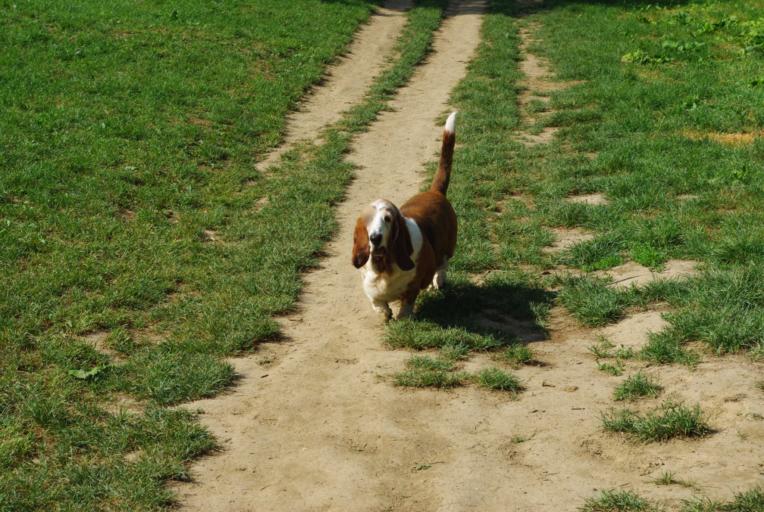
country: HU
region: Pest
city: Solymar
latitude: 47.5858
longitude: 18.9476
